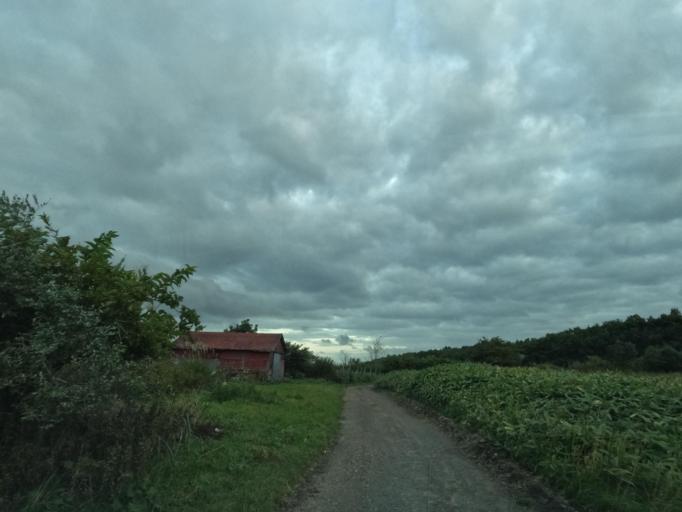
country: JP
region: Hokkaido
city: Muroran
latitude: 42.3711
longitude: 140.9705
